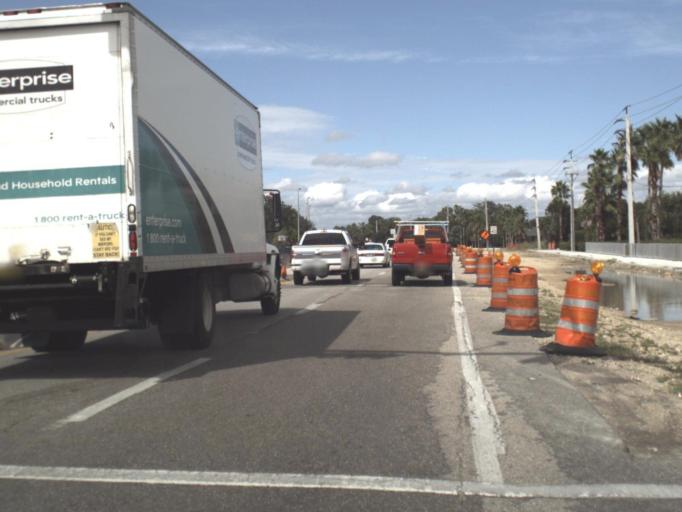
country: US
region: Florida
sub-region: Lee County
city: Fort Myers
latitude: 26.6047
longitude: -81.8505
